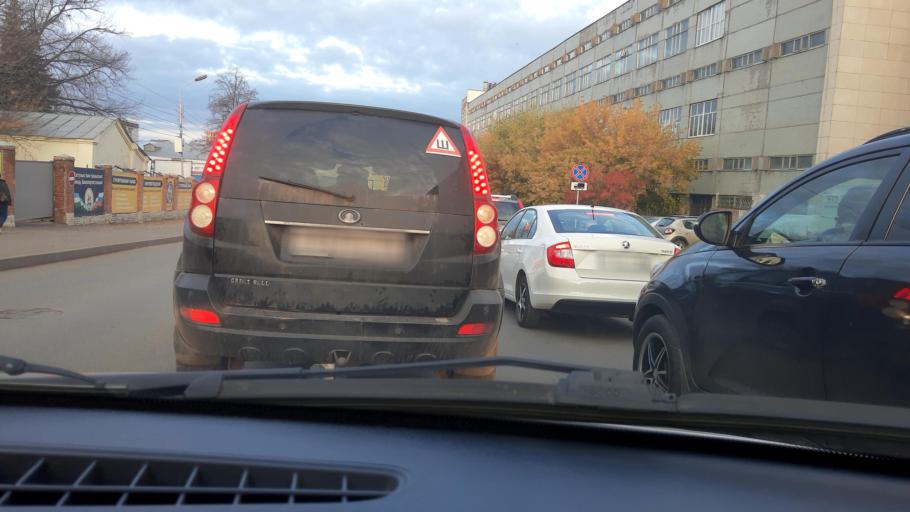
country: RU
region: Bashkortostan
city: Ufa
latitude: 54.7459
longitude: 55.9744
